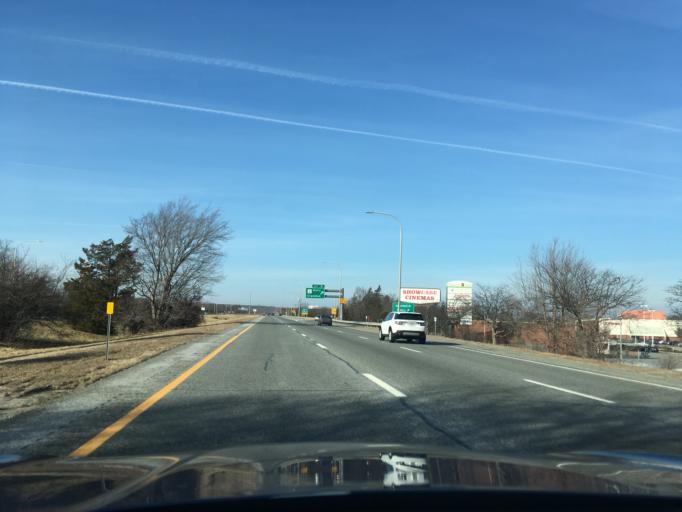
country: US
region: Rhode Island
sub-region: Kent County
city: West Warwick
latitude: 41.7206
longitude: -71.4776
